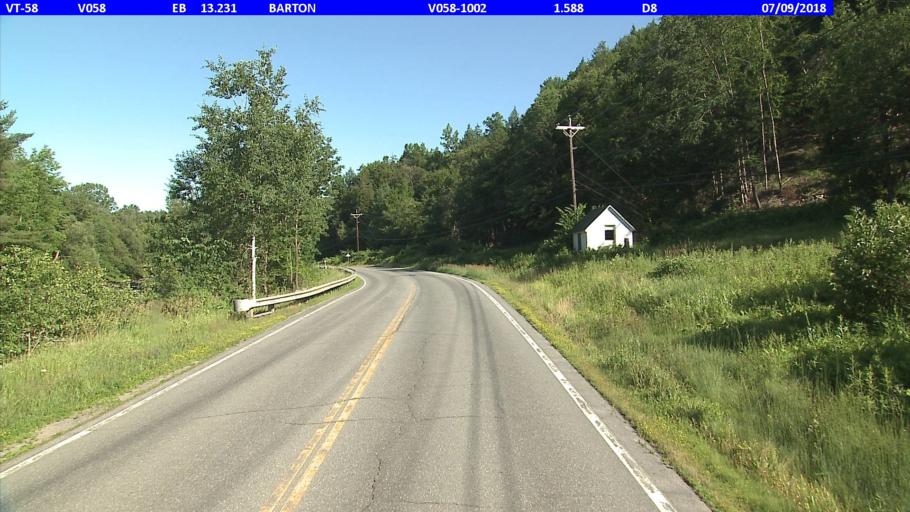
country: US
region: Vermont
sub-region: Orleans County
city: Newport
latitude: 44.8038
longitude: -72.1826
